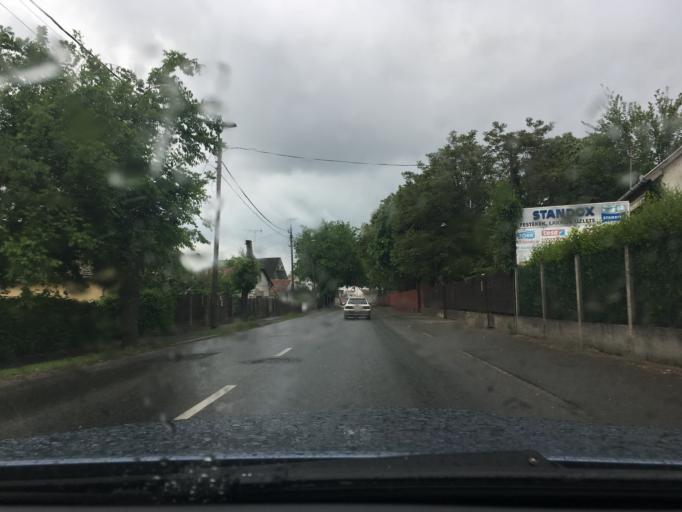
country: HU
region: Hajdu-Bihar
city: Debrecen
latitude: 47.5216
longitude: 21.6591
